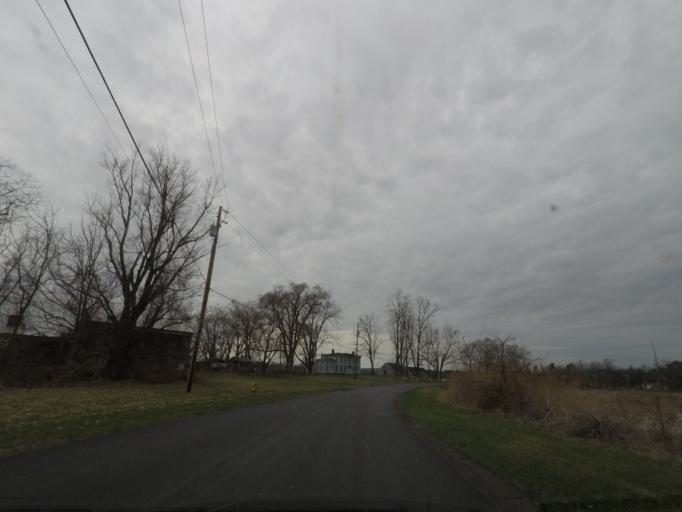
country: US
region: New York
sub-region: Rensselaer County
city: Castleton-on-Hudson
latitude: 42.5589
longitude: -73.7921
